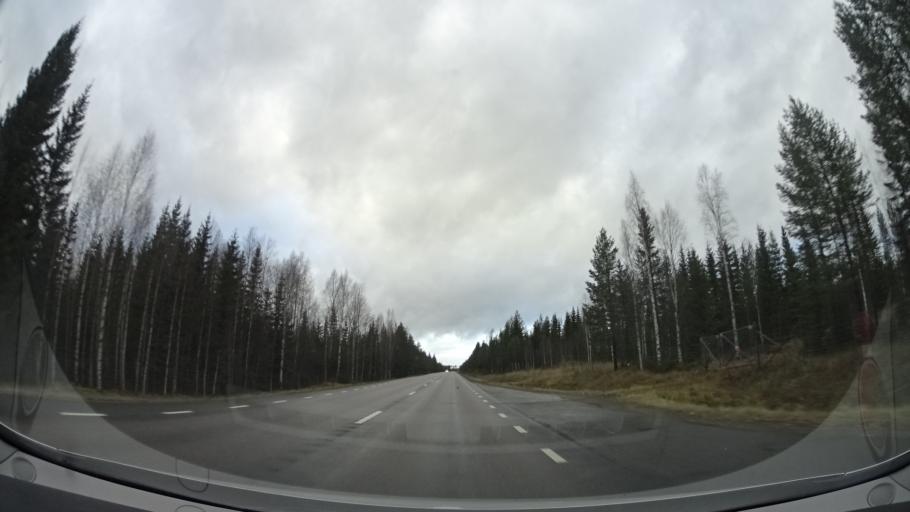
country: SE
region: Vaesterbotten
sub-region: Skelleftea Kommun
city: Viken
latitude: 64.7872
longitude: 20.7824
